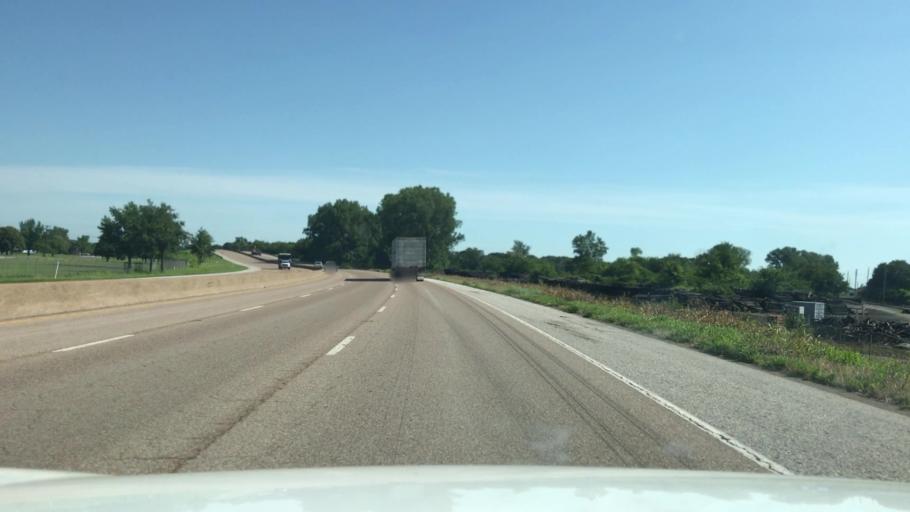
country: US
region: Illinois
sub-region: Madison County
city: Madison
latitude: 38.6930
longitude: -90.1682
